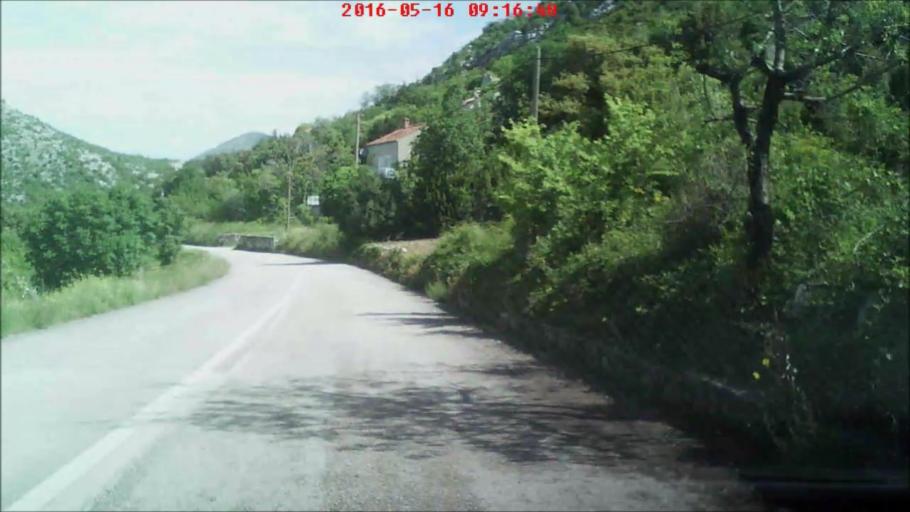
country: HR
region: Dubrovacko-Neretvanska
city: Podgora
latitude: 42.8521
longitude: 17.8366
